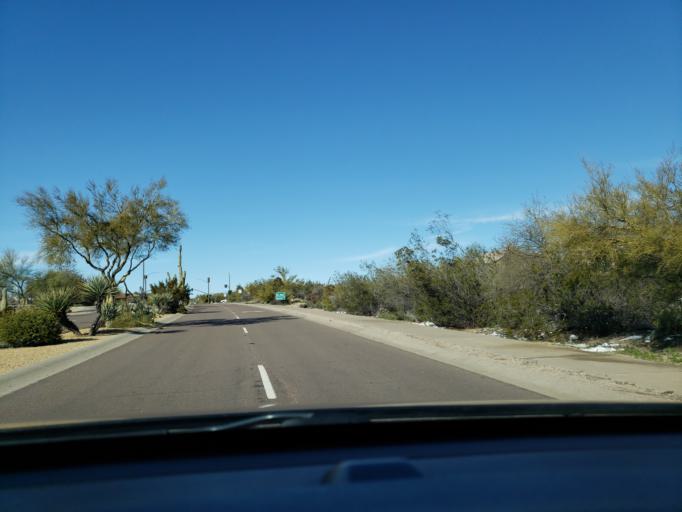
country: US
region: Arizona
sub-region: Maricopa County
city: Carefree
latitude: 33.7406
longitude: -111.8432
